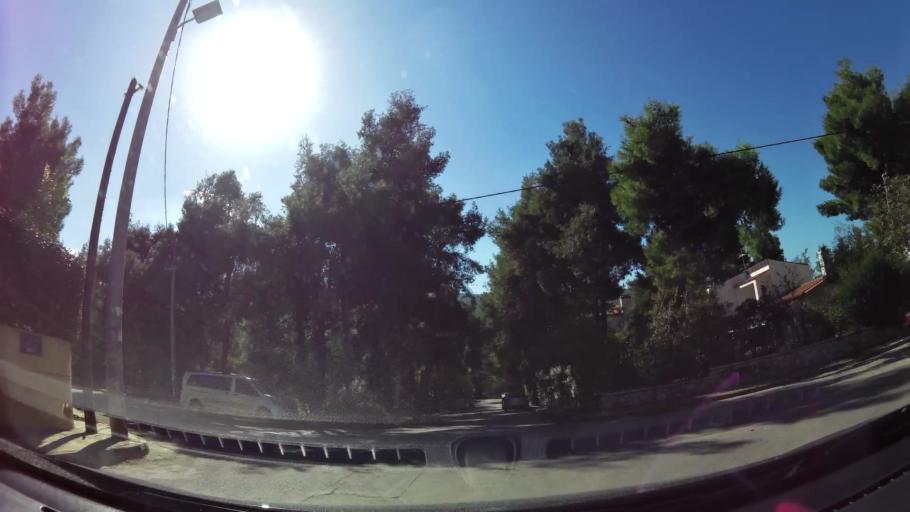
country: GR
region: Attica
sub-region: Nomarchia Anatolikis Attikis
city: Drosia
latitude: 38.1108
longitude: 23.8639
